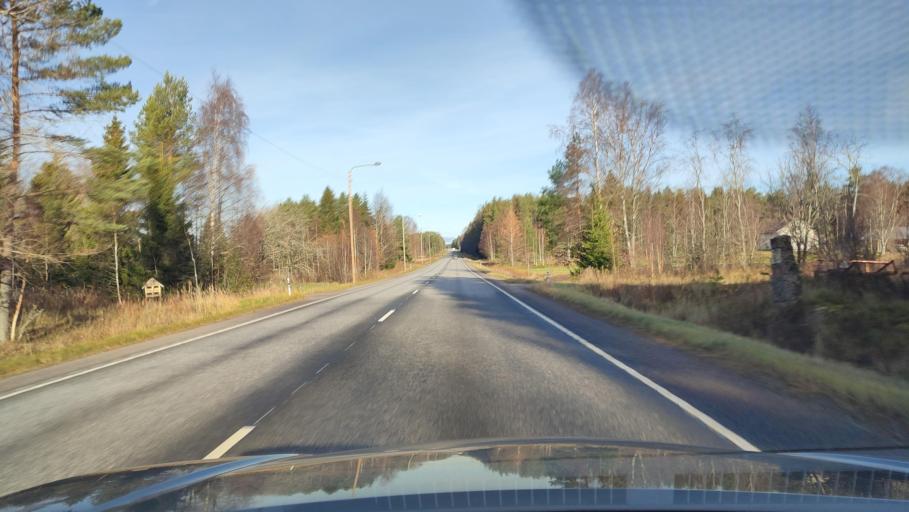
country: FI
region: Ostrobothnia
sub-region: Vaasa
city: Malax
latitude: 62.8072
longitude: 21.6803
